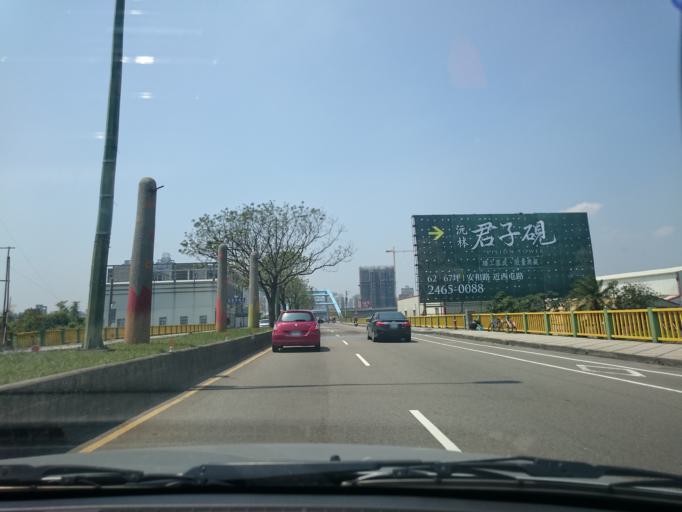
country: TW
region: Taiwan
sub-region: Taichung City
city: Taichung
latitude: 24.1802
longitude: 120.6320
